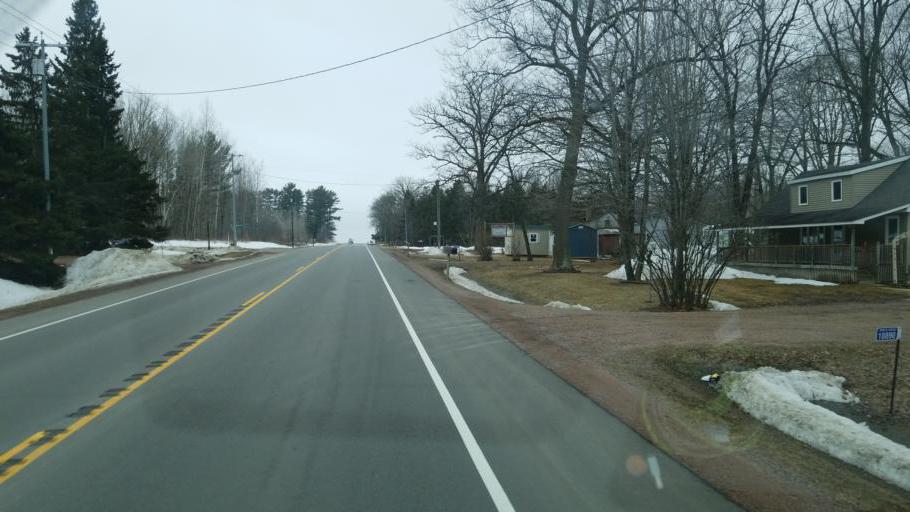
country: US
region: Wisconsin
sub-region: Wood County
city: Marshfield
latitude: 44.6564
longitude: -90.2580
